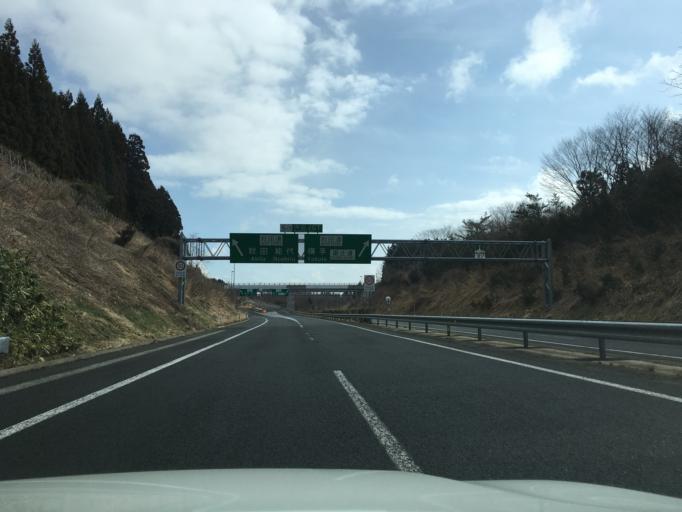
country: JP
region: Akita
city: Akita
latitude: 39.6387
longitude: 140.2057
